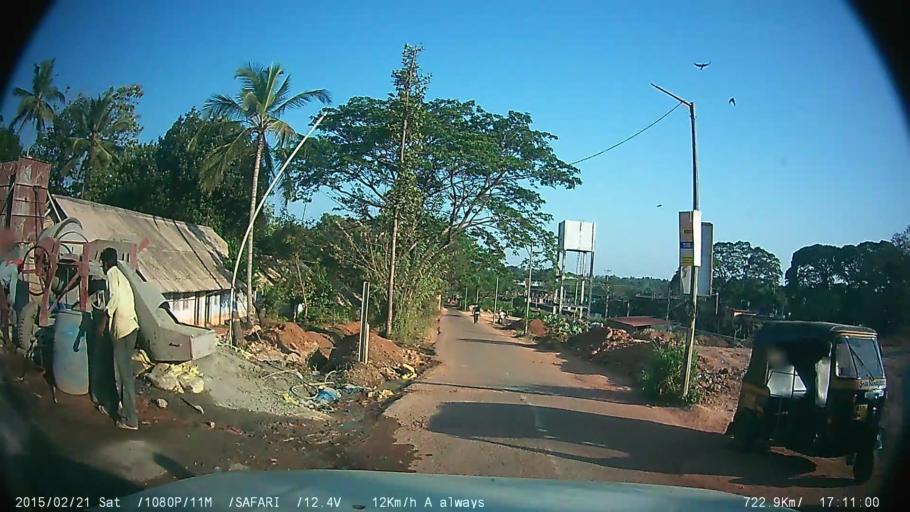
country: IN
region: Kerala
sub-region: Kottayam
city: Changanacheri
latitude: 9.4519
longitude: 76.5464
